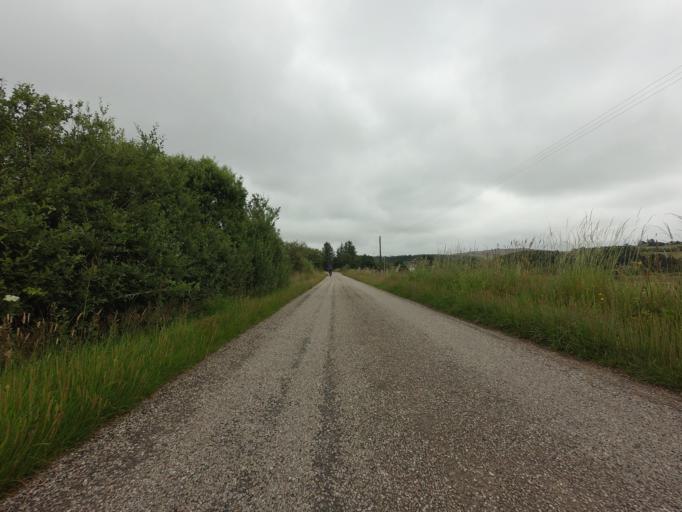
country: GB
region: Scotland
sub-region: Highland
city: Alness
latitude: 58.0070
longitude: -4.4047
